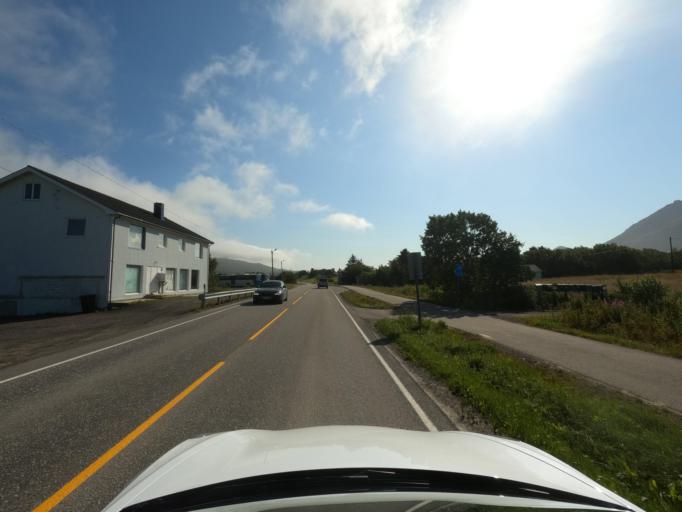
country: NO
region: Nordland
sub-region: Vestvagoy
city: Evjen
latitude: 68.2298
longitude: 13.7374
